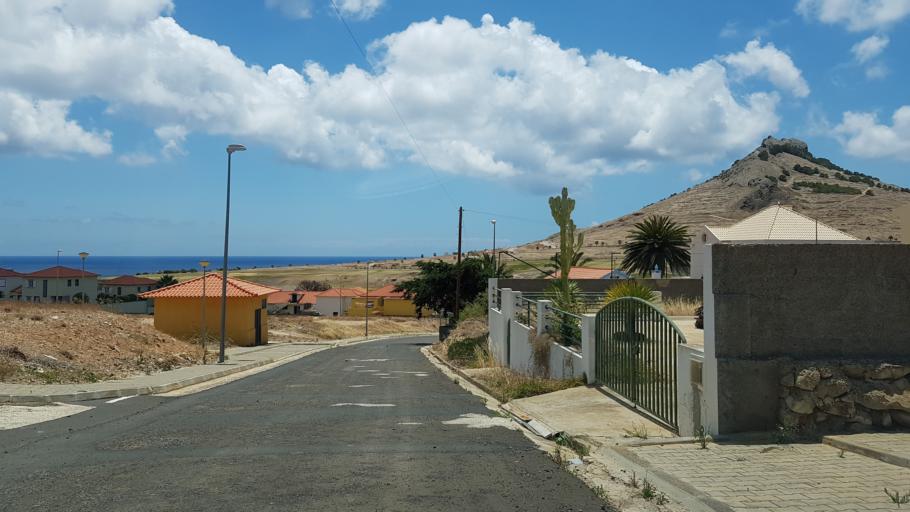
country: PT
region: Madeira
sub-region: Porto Santo
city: Vila de Porto Santo
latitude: 33.0565
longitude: -16.3660
